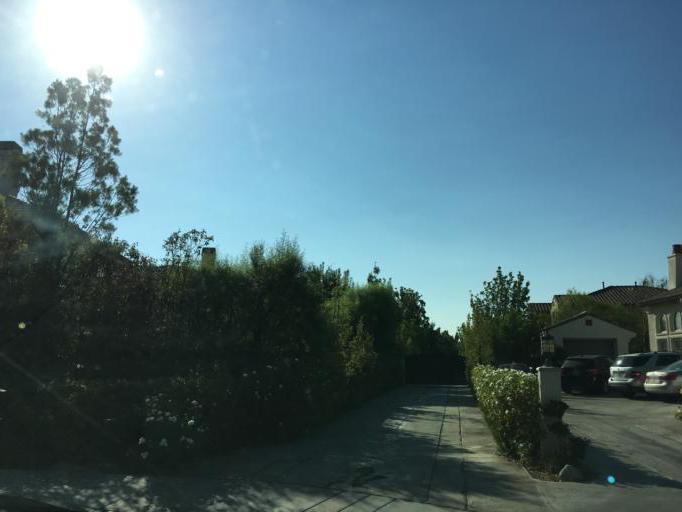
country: US
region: California
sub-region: Los Angeles County
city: Valencia
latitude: 34.4052
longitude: -118.5938
